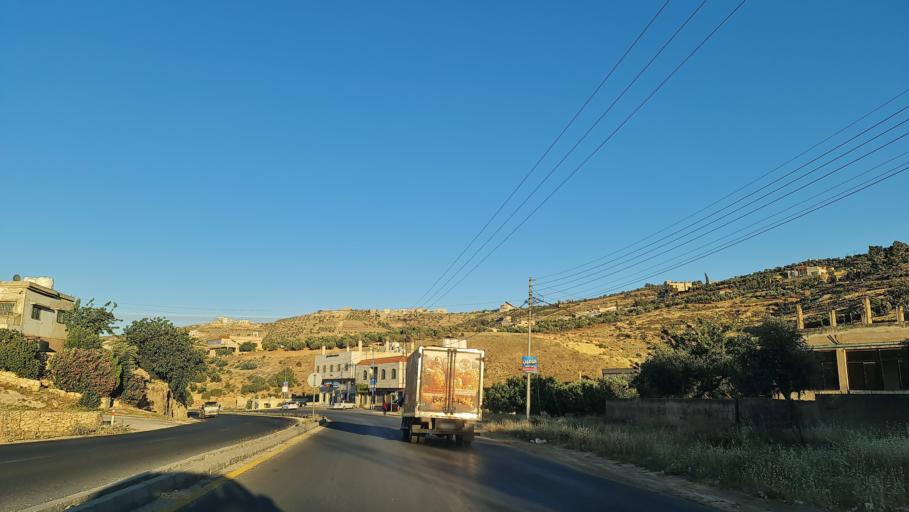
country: JO
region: Amman
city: Al Jubayhah
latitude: 32.0923
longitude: 35.9423
